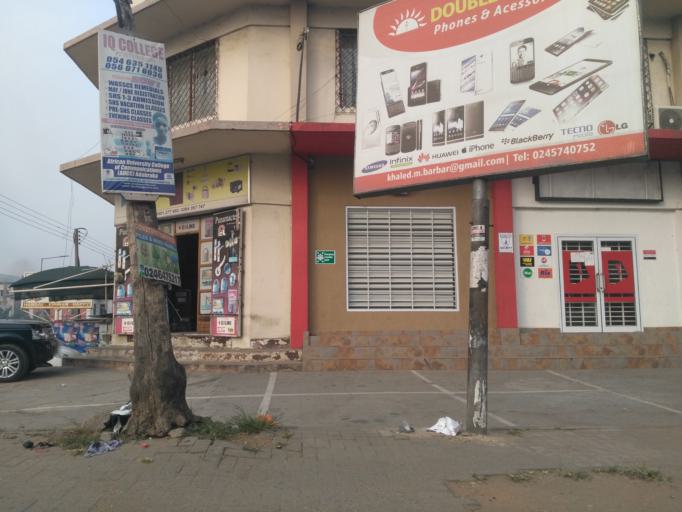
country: GH
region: Greater Accra
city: Accra
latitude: 5.5611
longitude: -0.2134
